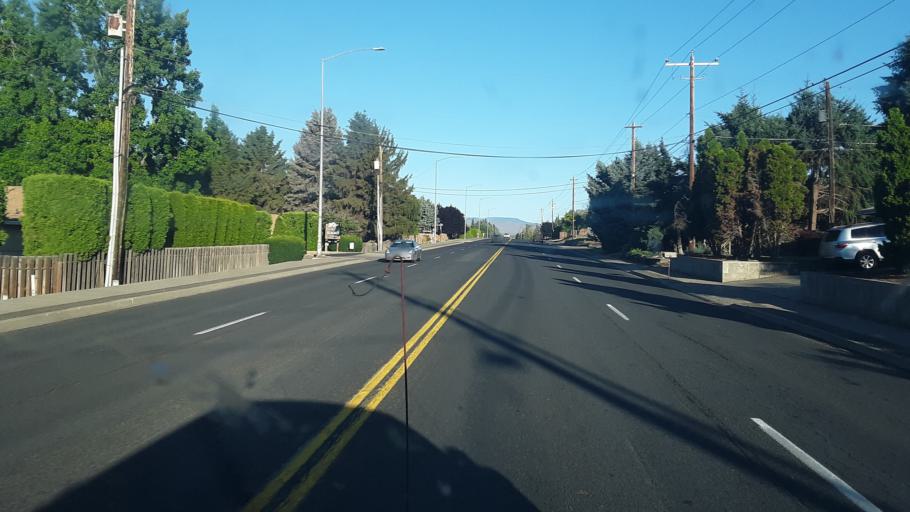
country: US
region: Washington
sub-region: Yakima County
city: West Valley
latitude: 46.6003
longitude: -120.6096
